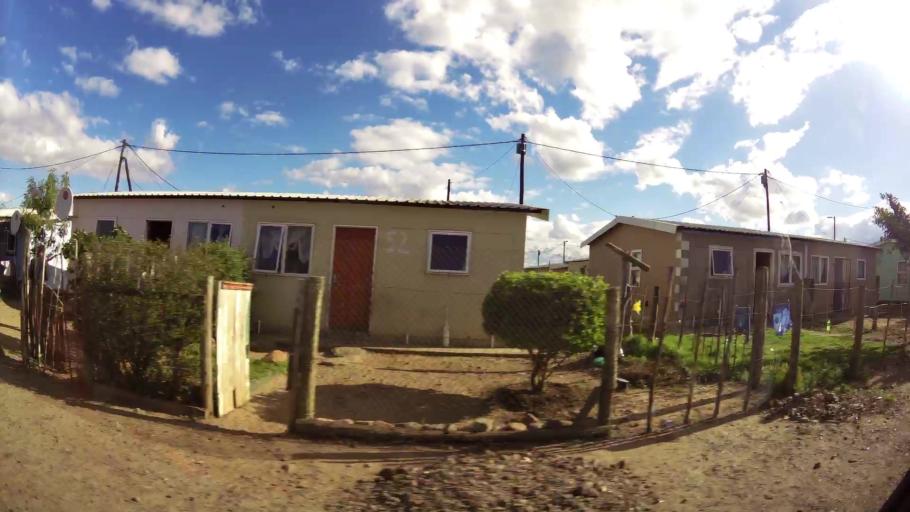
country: ZA
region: Western Cape
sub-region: Overberg District Municipality
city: Swellendam
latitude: -34.0470
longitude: 20.4404
